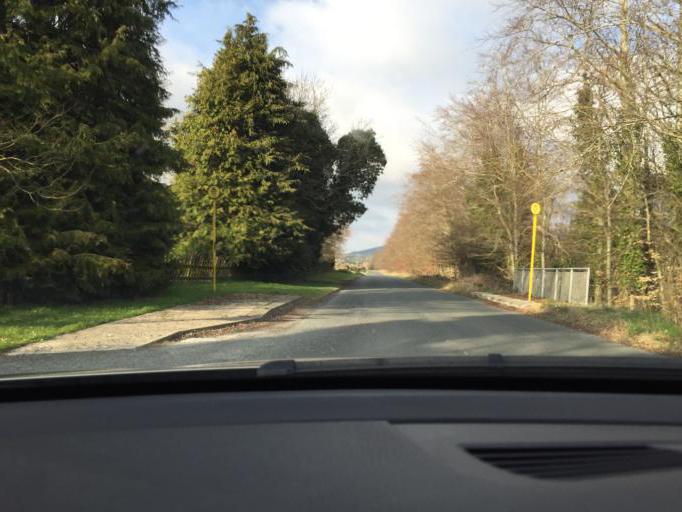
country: IE
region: Leinster
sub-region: Wicklow
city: Valleymount
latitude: 53.1207
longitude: -6.5363
